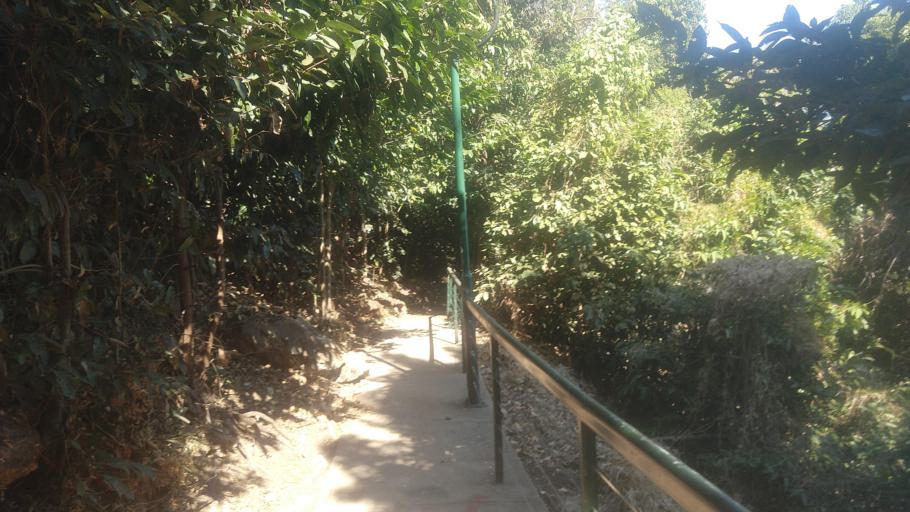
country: AU
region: Northern Territory
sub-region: Darwin
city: Darwin
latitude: -12.4649
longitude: 130.8390
